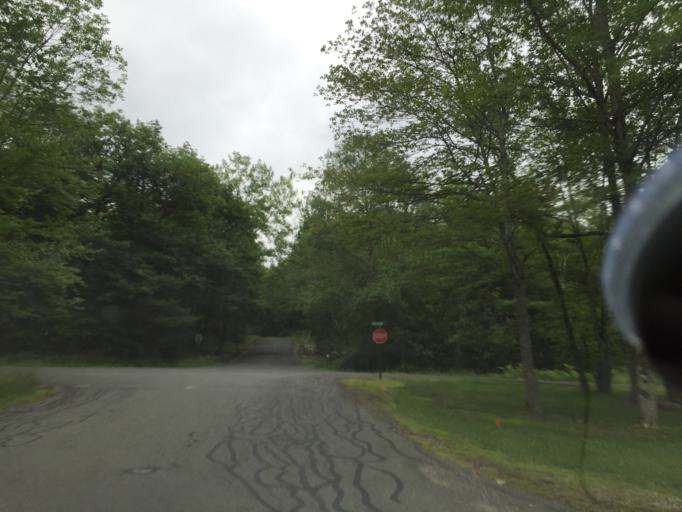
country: US
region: Connecticut
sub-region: Litchfield County
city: Litchfield
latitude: 41.8153
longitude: -73.2504
